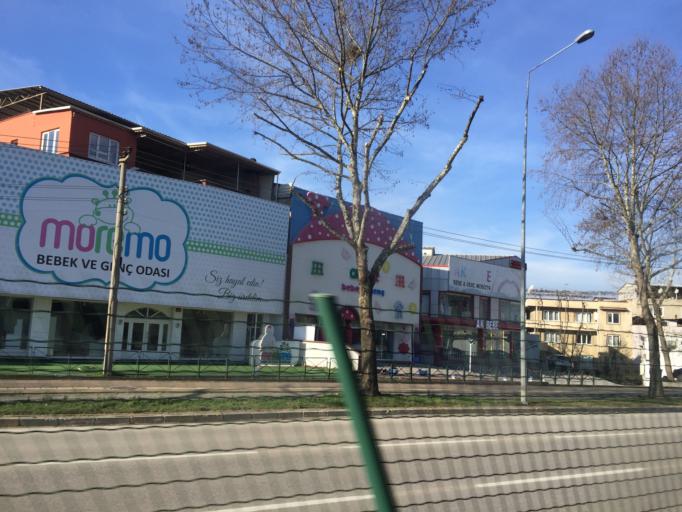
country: TR
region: Bursa
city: Yildirim
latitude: 40.2210
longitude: 28.9960
